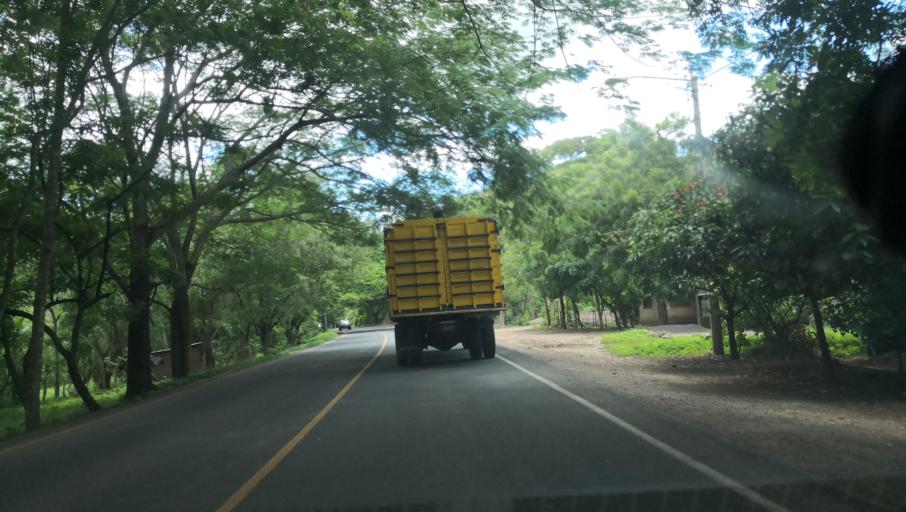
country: NI
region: Madriz
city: Yalaguina
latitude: 13.4761
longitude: -86.4819
